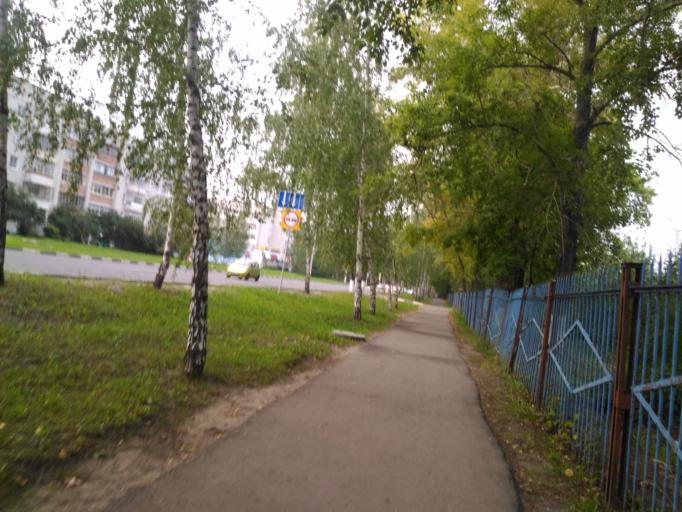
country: RU
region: Ulyanovsk
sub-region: Ulyanovskiy Rayon
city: Ulyanovsk
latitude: 54.2670
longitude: 48.3349
